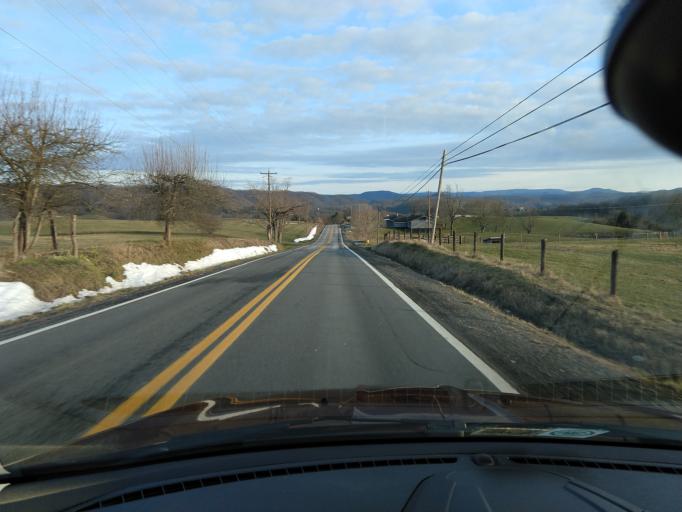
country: US
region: West Virginia
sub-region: Greenbrier County
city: Lewisburg
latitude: 37.9582
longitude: -80.3783
